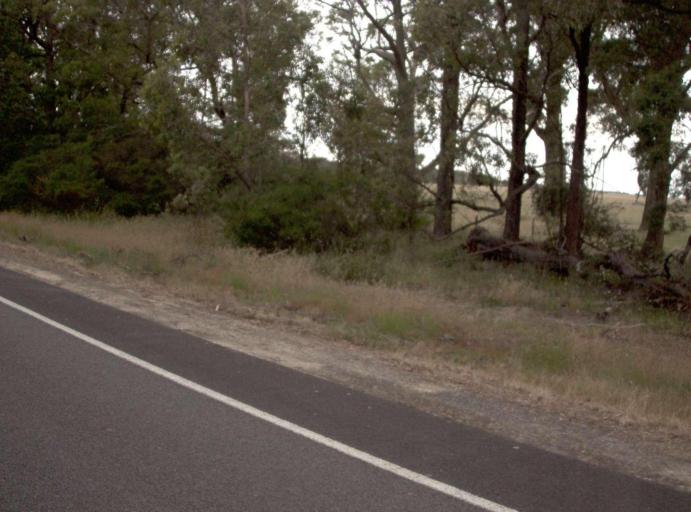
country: AU
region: Victoria
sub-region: Wellington
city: Sale
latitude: -38.5081
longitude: 146.8908
